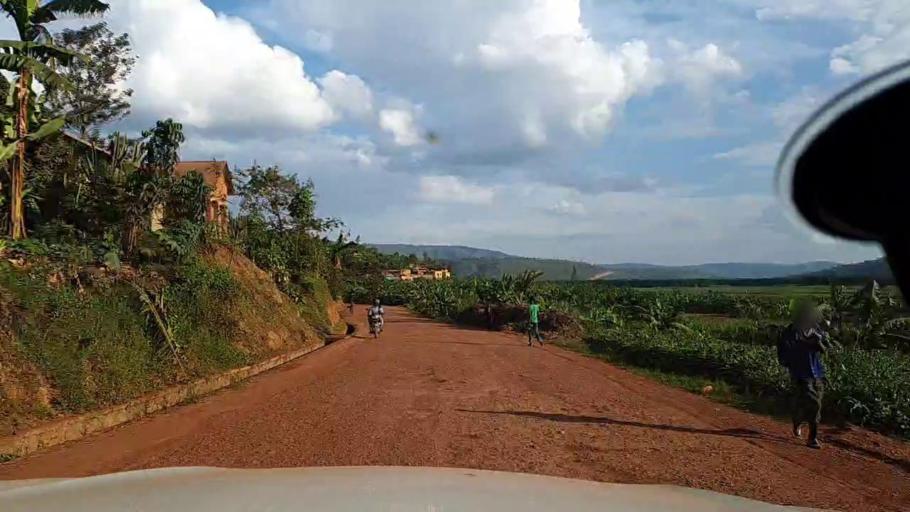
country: RW
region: Kigali
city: Kigali
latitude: -1.9268
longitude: 29.9912
